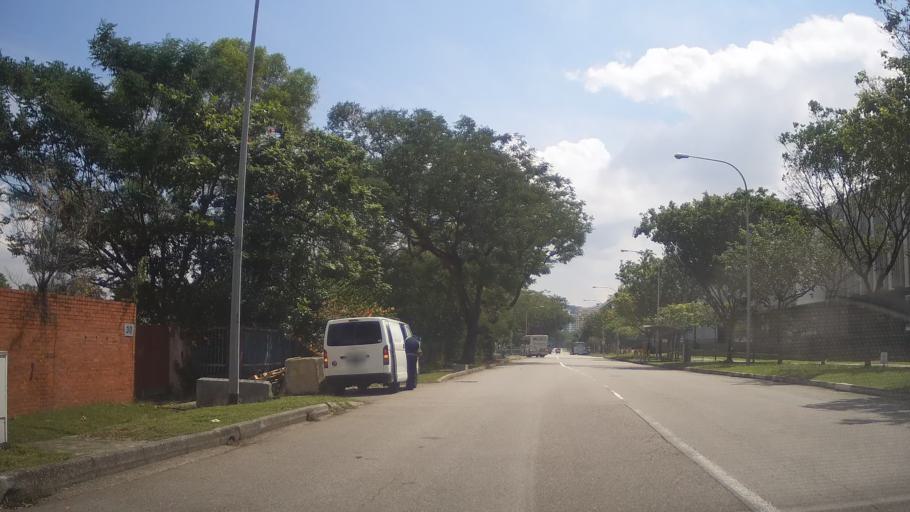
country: SG
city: Singapore
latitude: 1.3259
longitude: 103.7115
